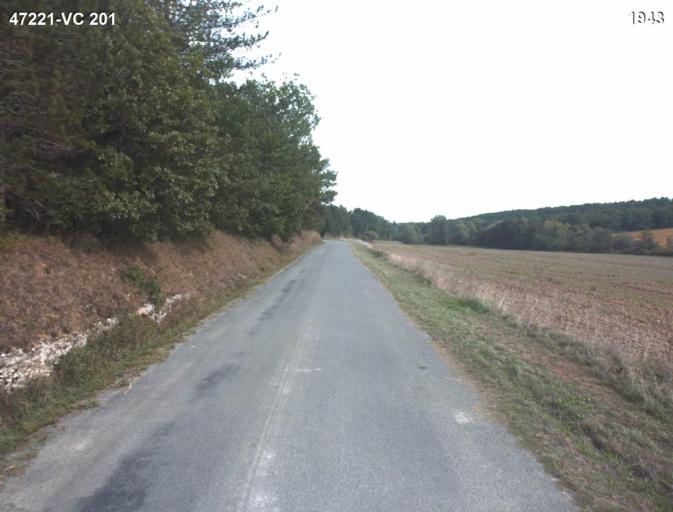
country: FR
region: Aquitaine
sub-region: Departement du Lot-et-Garonne
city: Mezin
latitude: 44.1106
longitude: 0.2424
